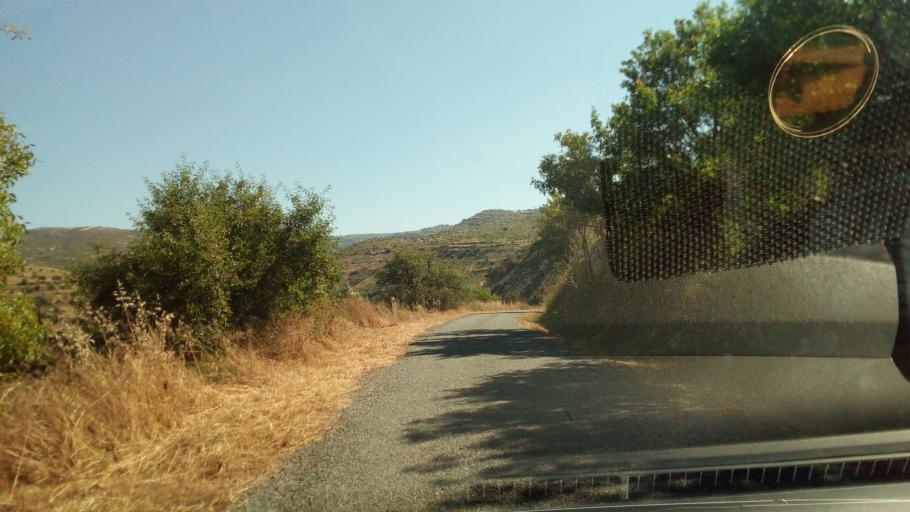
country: CY
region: Limassol
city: Pachna
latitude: 34.8135
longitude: 32.7468
